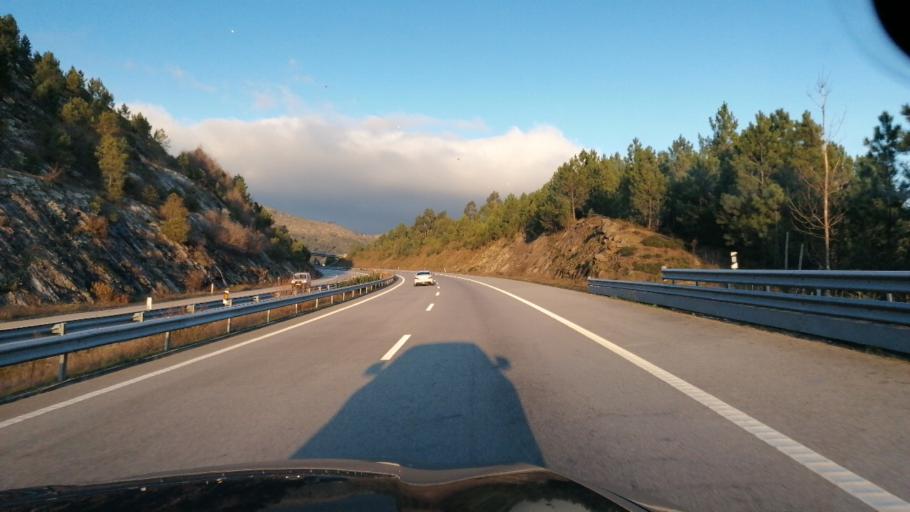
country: PT
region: Vila Real
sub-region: Ribeira de Pena
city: Ribeira de Pena
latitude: 41.4783
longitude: -7.8710
